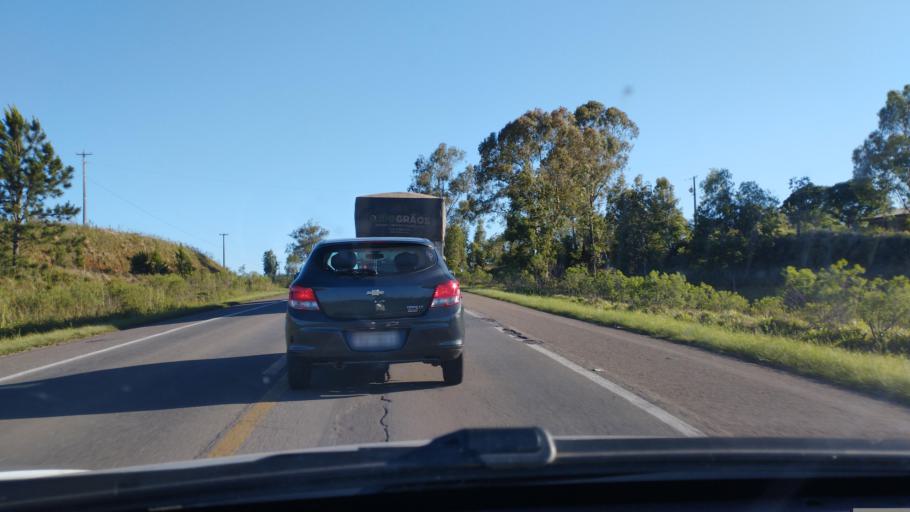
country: BR
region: Rio Grande do Sul
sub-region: Julio De Castilhos
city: Julio de Castilhos
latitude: -29.3759
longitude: -53.6708
